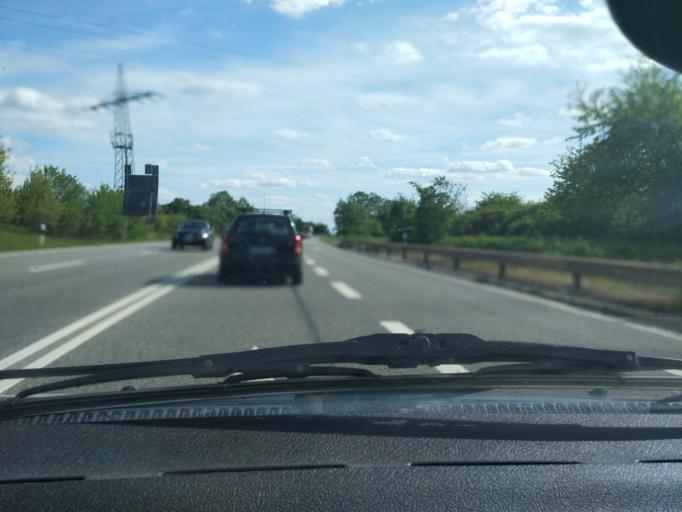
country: DE
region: Rheinland-Pfalz
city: Munster-Sarmsheim
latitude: 49.9358
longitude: 7.9159
